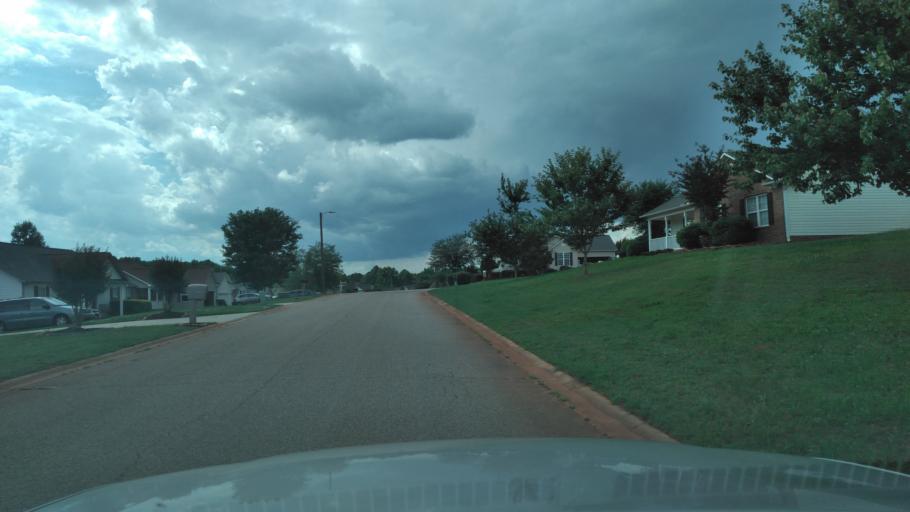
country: US
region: South Carolina
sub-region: Spartanburg County
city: Boiling Springs
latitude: 35.0847
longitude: -81.9402
